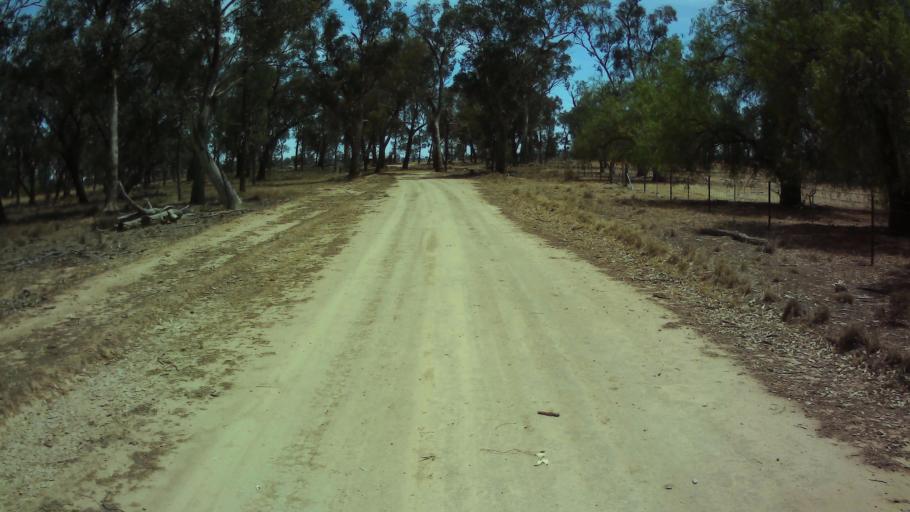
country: AU
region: New South Wales
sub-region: Weddin
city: Grenfell
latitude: -34.0336
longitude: 147.9339
